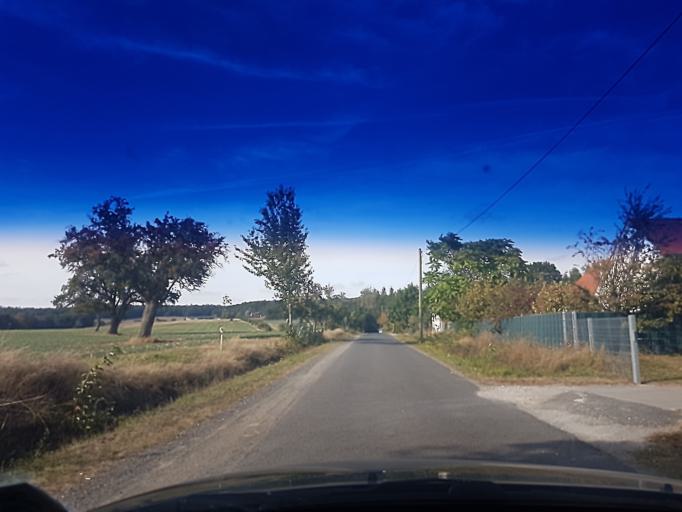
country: DE
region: Bavaria
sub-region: Regierungsbezirk Mittelfranken
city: Burghaslach
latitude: 49.7774
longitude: 10.5442
